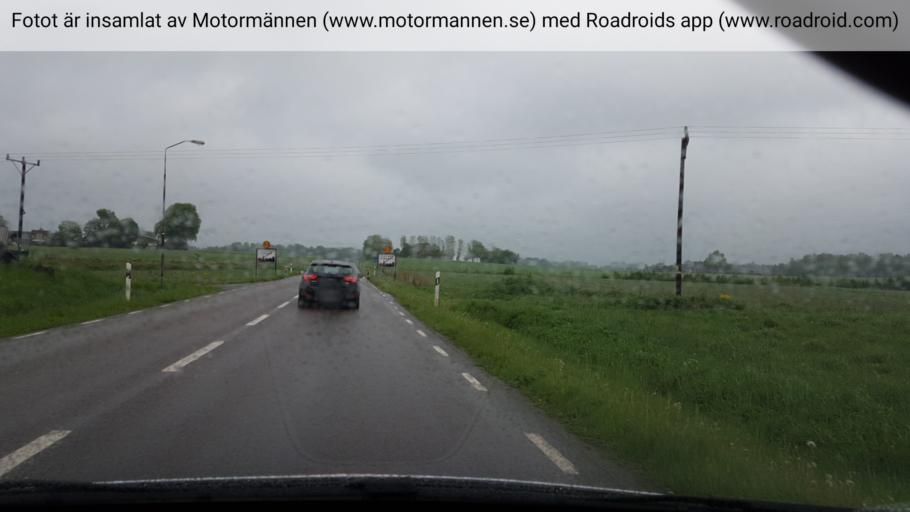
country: SE
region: Vaestra Goetaland
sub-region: Falkopings Kommun
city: Falkoeping
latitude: 58.0884
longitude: 13.5238
